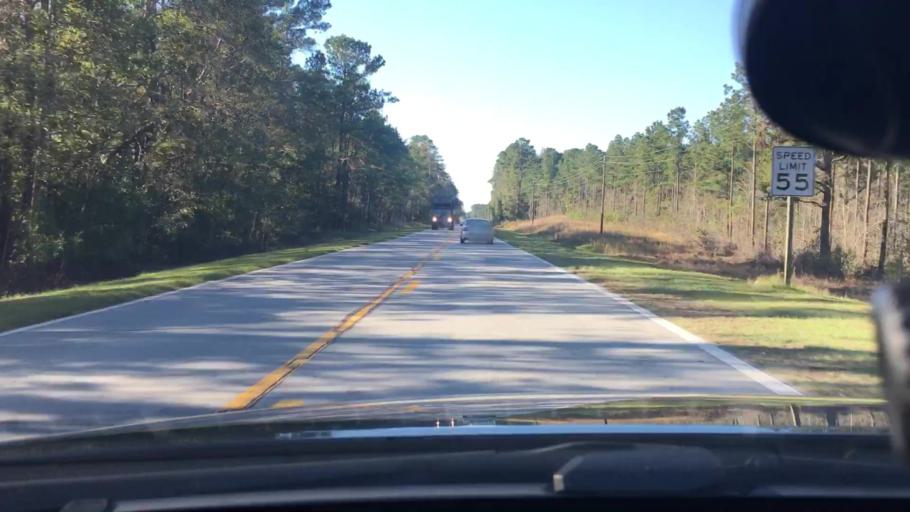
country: US
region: North Carolina
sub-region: Craven County
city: Vanceboro
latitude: 35.2189
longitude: -77.1227
